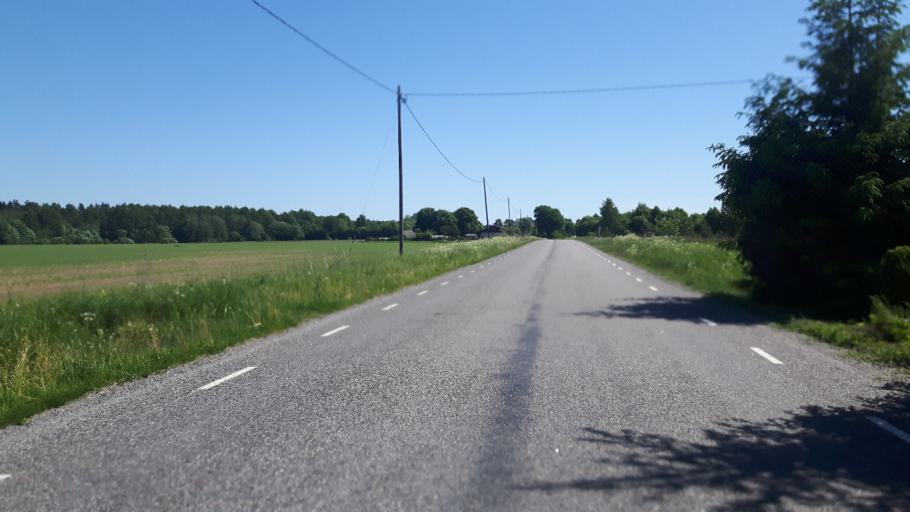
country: EE
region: Raplamaa
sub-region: Kohila vald
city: Kohila
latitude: 59.1917
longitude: 24.7058
